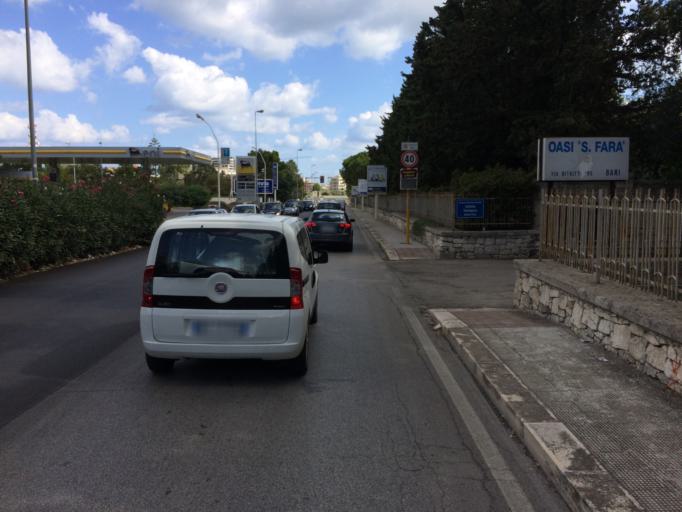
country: IT
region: Apulia
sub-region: Provincia di Bari
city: Bari
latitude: 41.1004
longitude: 16.8465
